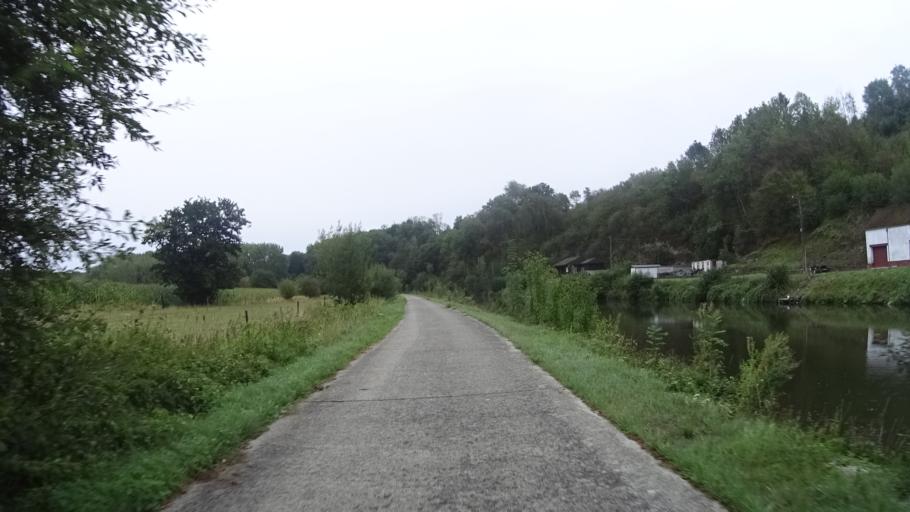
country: BE
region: Wallonia
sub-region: Province du Hainaut
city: Merbes-le-Chateau
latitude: 50.3197
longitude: 4.2180
